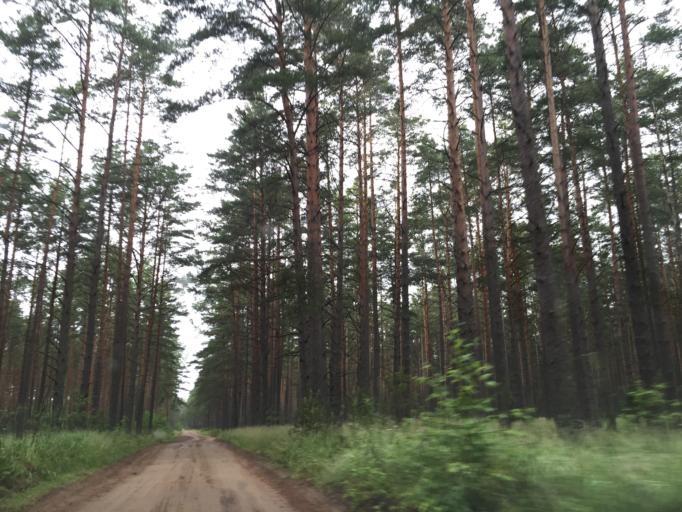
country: LV
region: Riga
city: Jaunciems
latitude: 57.0496
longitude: 24.2066
